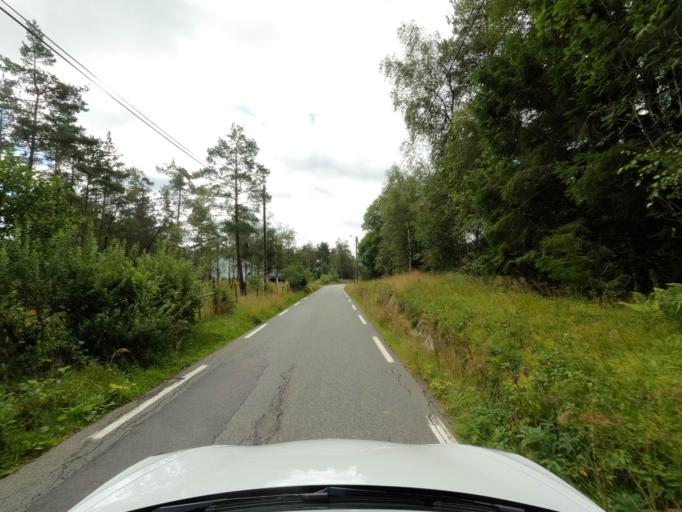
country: NO
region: Hordaland
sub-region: Bergen
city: Espeland
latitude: 60.3099
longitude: 5.5037
